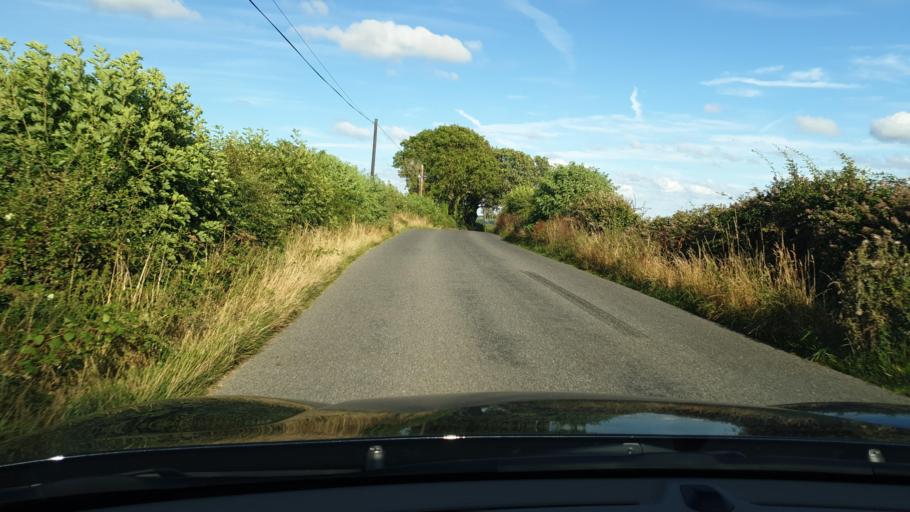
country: IE
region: Leinster
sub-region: An Mhi
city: Stamullin
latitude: 53.6151
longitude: -6.3113
